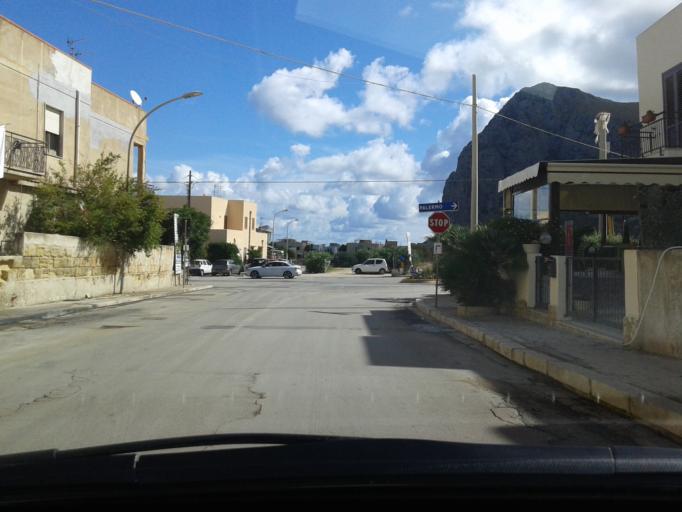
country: IT
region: Sicily
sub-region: Trapani
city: San Vito Lo Capo
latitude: 38.1672
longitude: 12.7346
